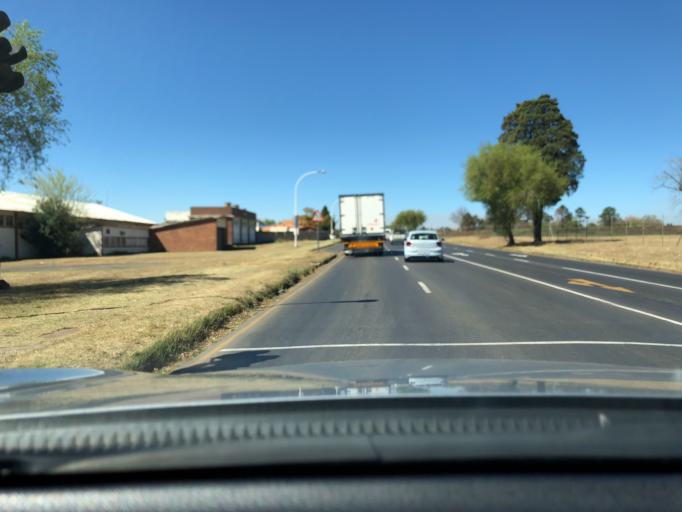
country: ZA
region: KwaZulu-Natal
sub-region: Amajuba District Municipality
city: Newcastle
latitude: -27.7578
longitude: 29.9433
